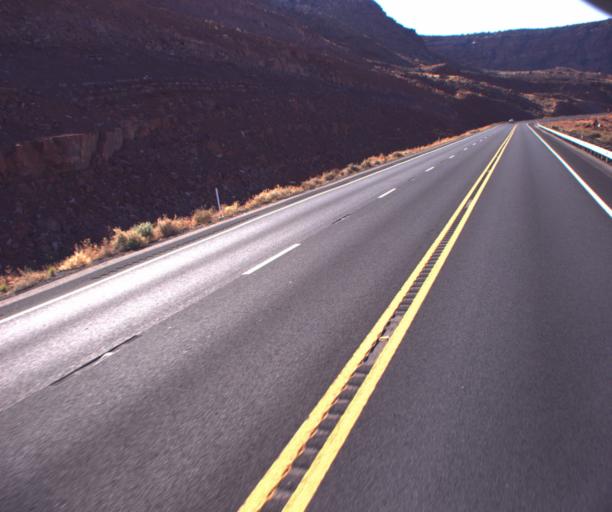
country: US
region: Arizona
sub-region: Coconino County
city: LeChee
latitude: 36.6543
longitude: -111.6325
